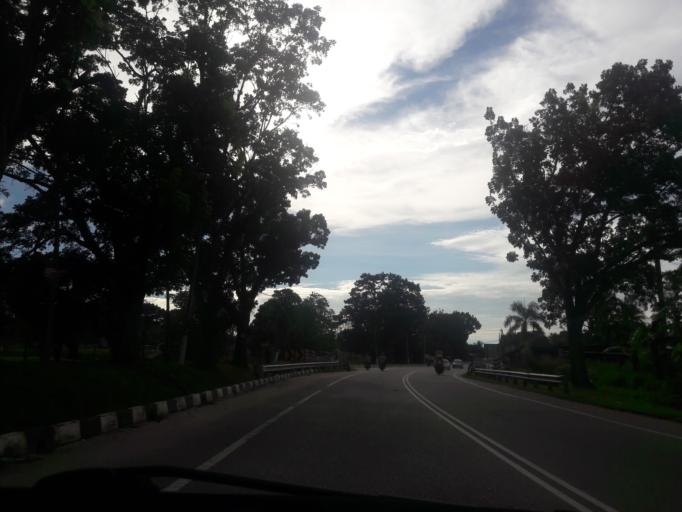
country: MY
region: Kedah
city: Sungai Petani
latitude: 5.6306
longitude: 100.5219
